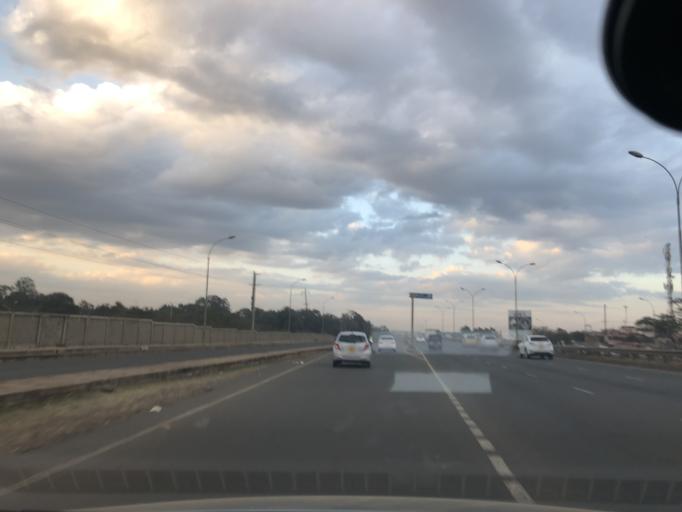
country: KE
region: Kiambu
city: Kiambu
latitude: -1.1909
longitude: 36.9287
